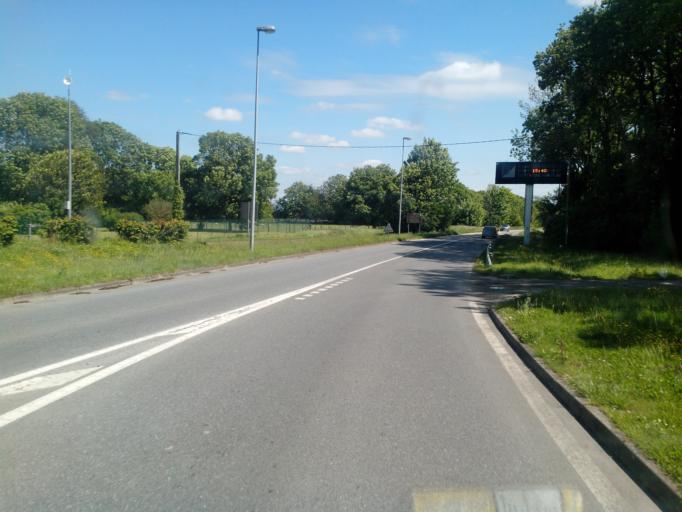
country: FR
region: Haute-Normandie
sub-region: Departement de la Seine-Maritime
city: La Cerlangue
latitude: 49.4967
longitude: 0.4354
